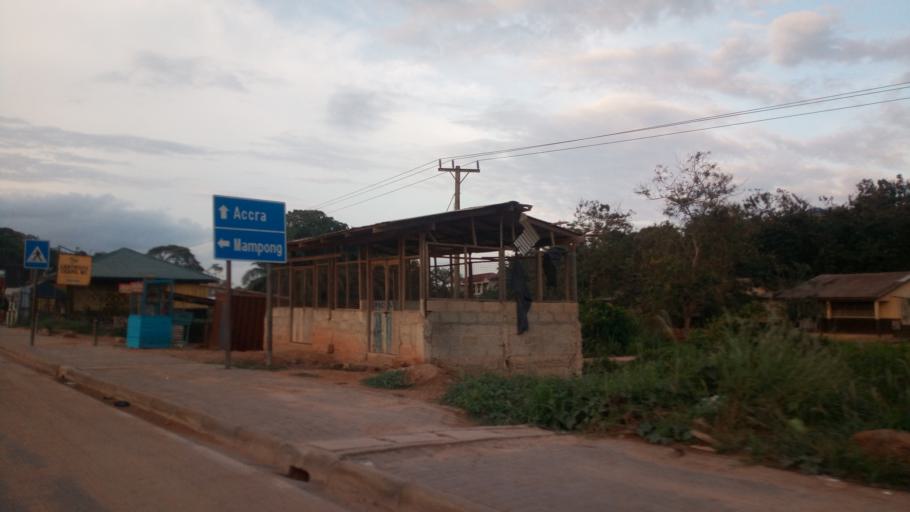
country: GH
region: Western
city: Sekondi-Takoradi
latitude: 4.9503
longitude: -1.7614
